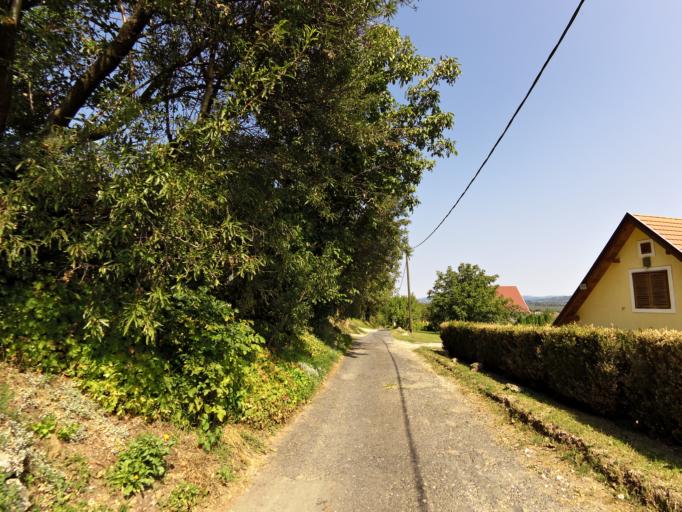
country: HU
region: Zala
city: Vonyarcvashegy
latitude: 46.7958
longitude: 17.3720
